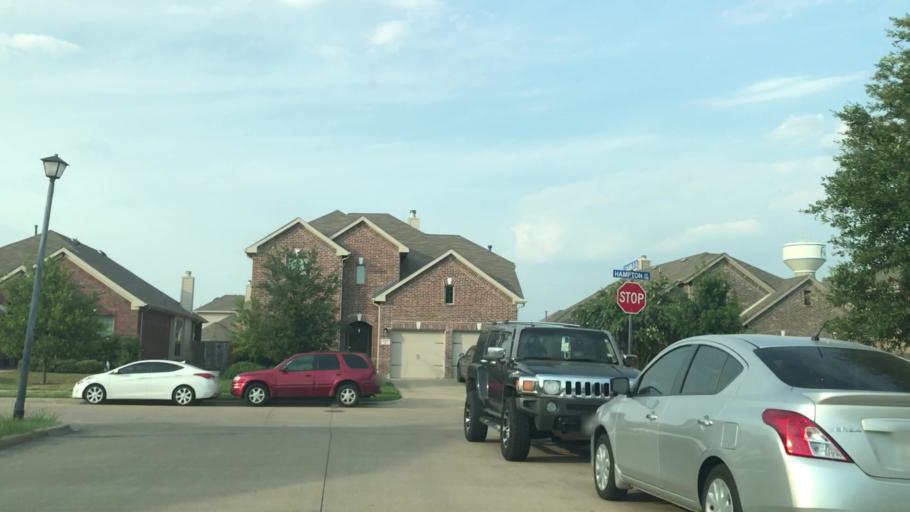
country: US
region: Texas
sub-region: Rockwall County
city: Fate
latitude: 32.9405
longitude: -96.3899
